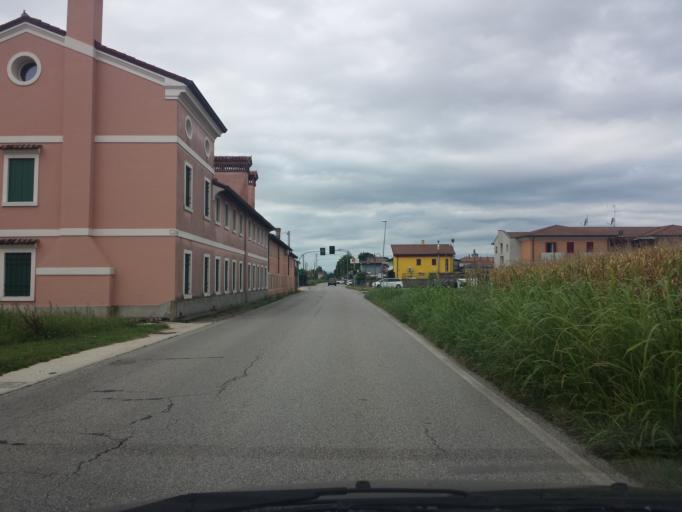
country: IT
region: Veneto
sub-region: Provincia di Padova
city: Galliera Veneta
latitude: 45.6696
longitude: 11.8027
